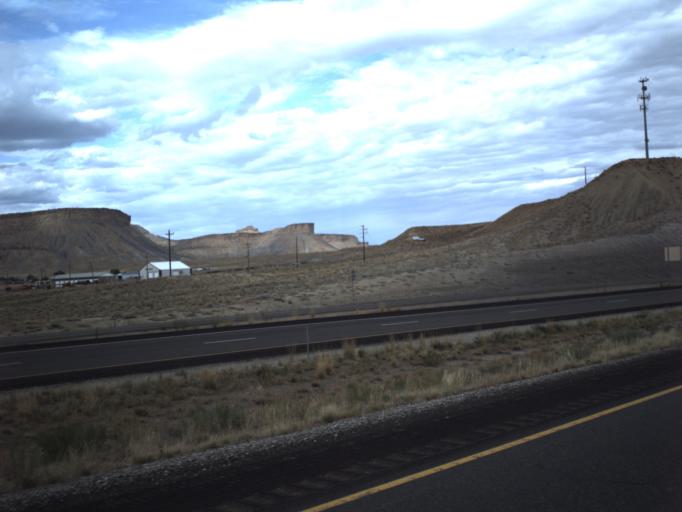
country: US
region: Utah
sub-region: Grand County
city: Moab
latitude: 38.9618
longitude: -109.7192
